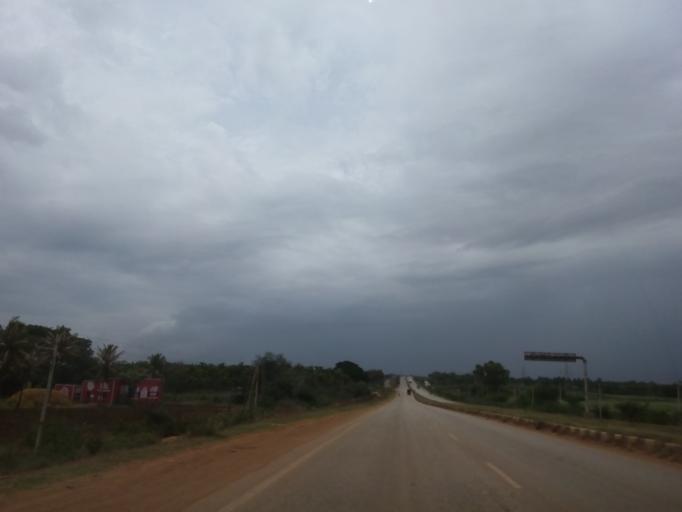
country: IN
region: Karnataka
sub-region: Davanagere
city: Harihar
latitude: 14.4857
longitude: 75.7932
